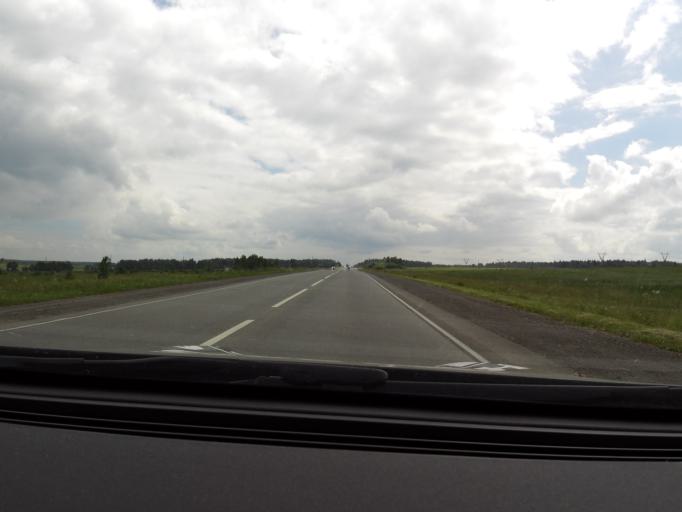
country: RU
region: Perm
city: Orda
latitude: 57.2915
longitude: 56.9922
